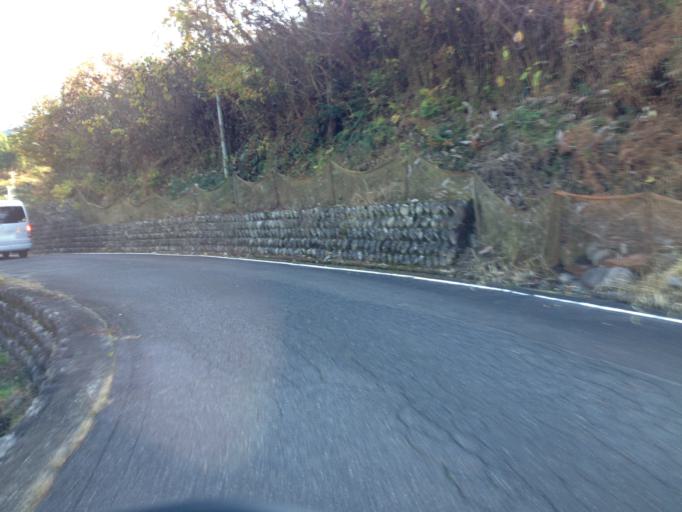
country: JP
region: Gifu
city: Mitake
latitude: 35.6074
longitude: 137.2017
